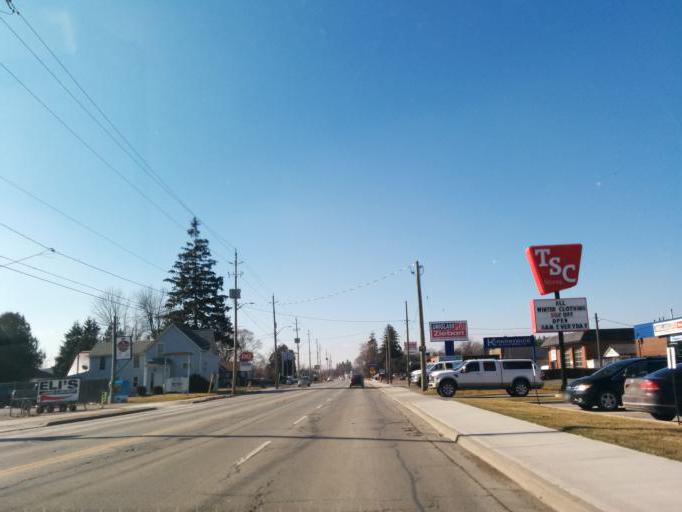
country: CA
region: Ontario
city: Norfolk County
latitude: 42.8445
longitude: -80.3165
